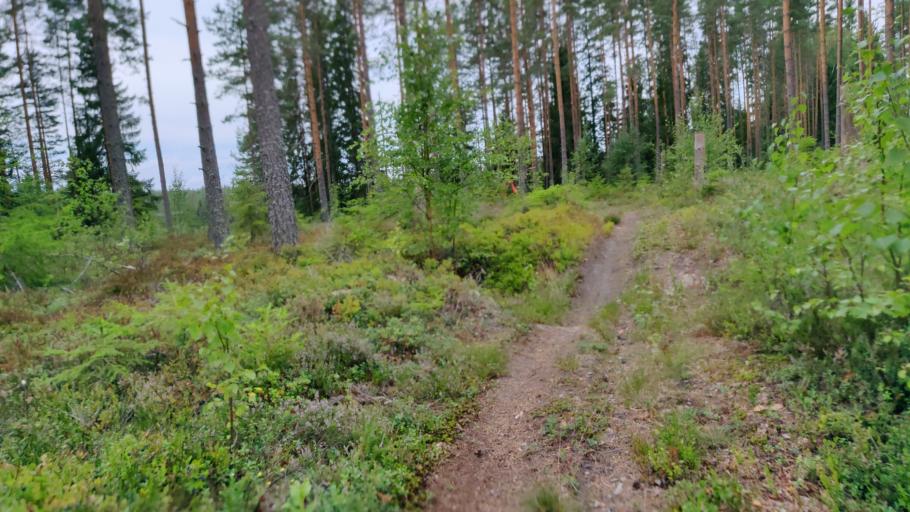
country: SE
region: Vaermland
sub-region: Hagfors Kommun
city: Hagfors
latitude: 60.0203
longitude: 13.5459
